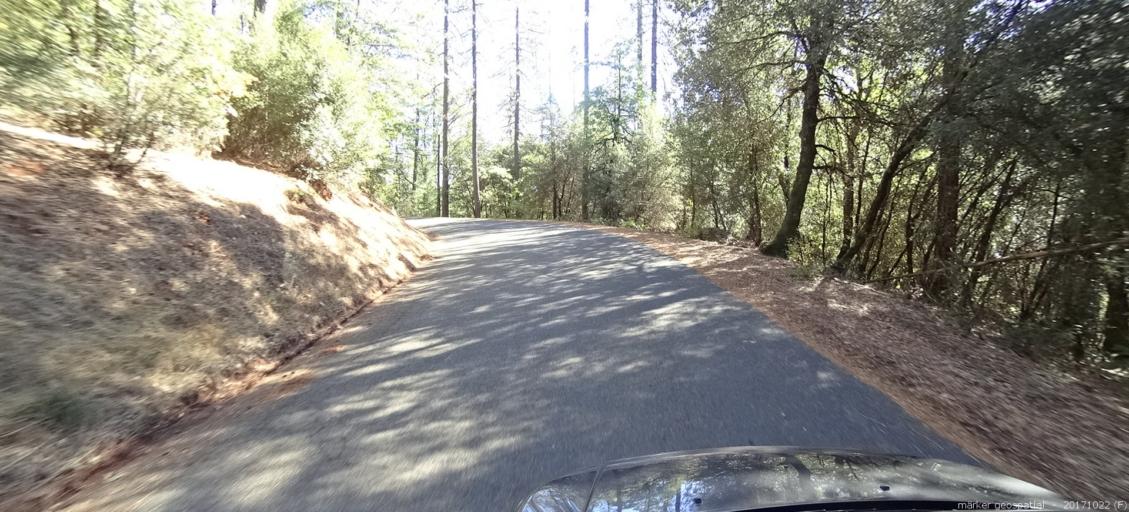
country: US
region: California
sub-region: Shasta County
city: Central Valley (historical)
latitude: 40.9429
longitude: -122.4414
